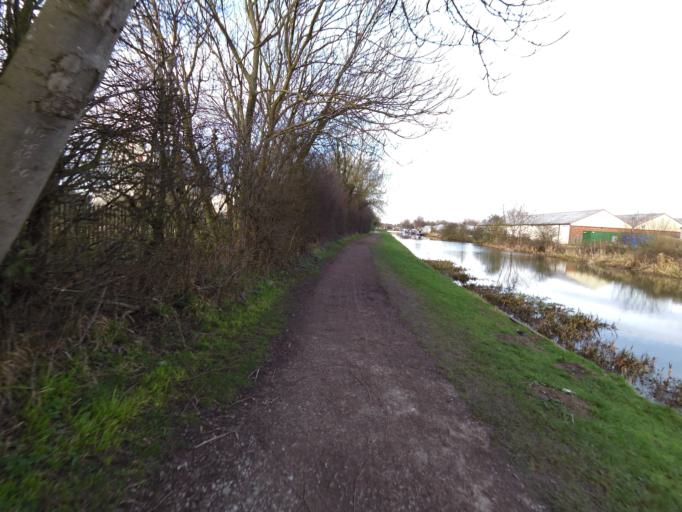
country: GB
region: England
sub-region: North Yorkshire
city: Selby
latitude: 53.7742
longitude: -1.0666
